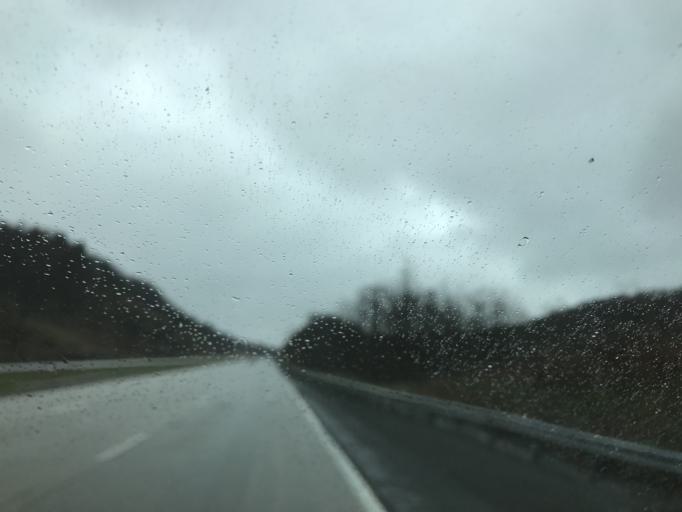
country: US
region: West Virginia
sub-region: Greenbrier County
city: Rainelle
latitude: 37.8330
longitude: -80.7725
